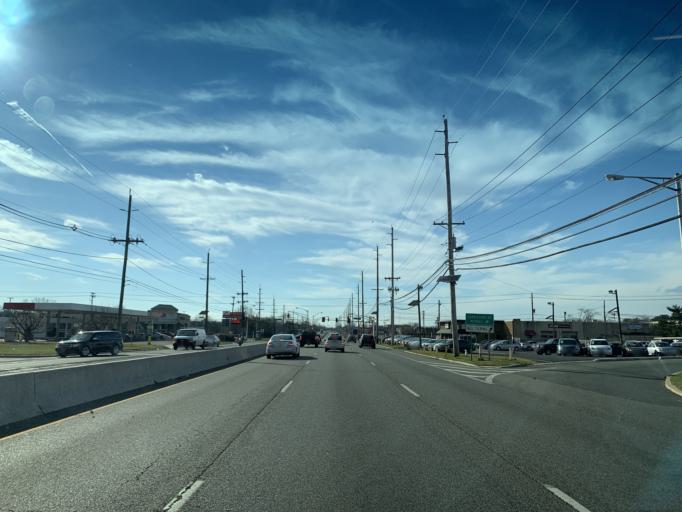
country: US
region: New Jersey
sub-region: Burlington County
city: Edgewater Park
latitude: 40.0475
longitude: -74.9022
